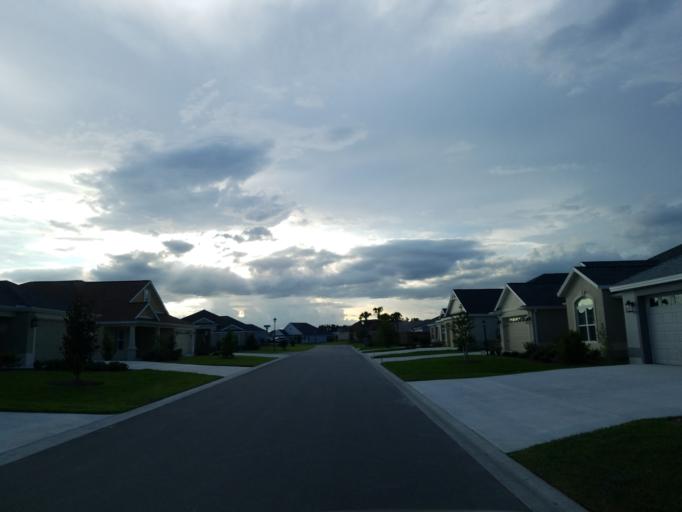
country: US
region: Florida
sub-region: Sumter County
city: Wildwood
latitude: 28.7949
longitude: -82.0250
